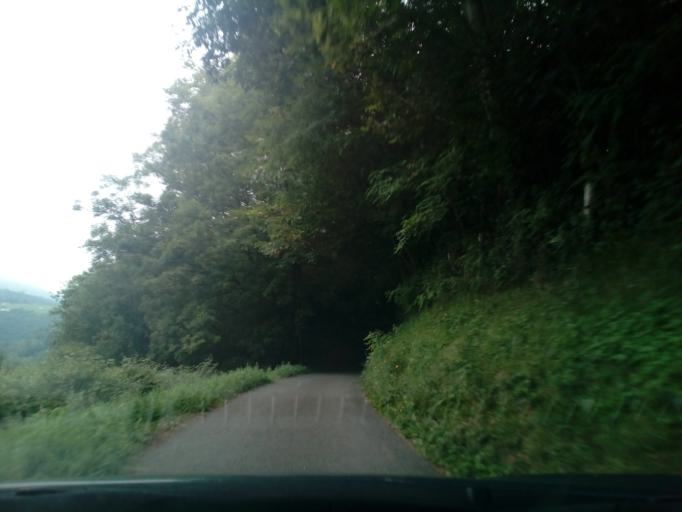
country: ES
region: Basque Country
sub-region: Provincia de Guipuzcoa
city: Andoain
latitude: 43.2148
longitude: -2.0102
